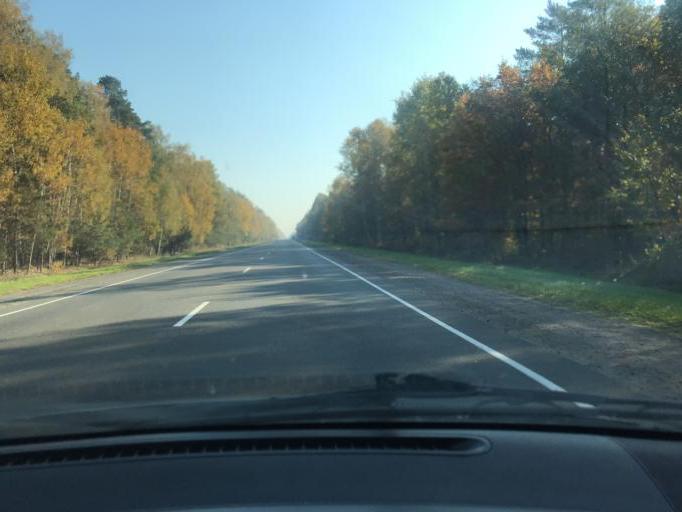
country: BY
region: Brest
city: Horad Luninyets
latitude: 52.3060
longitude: 26.6939
